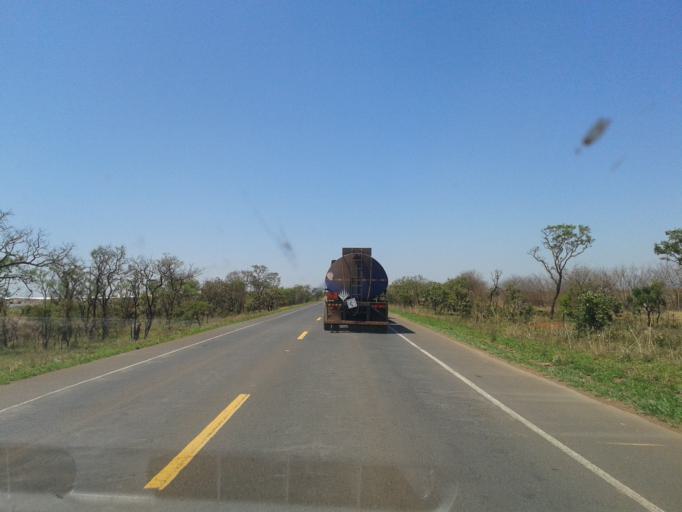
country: BR
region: Minas Gerais
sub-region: Araxa
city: Araxa
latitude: -19.3062
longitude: -47.3936
